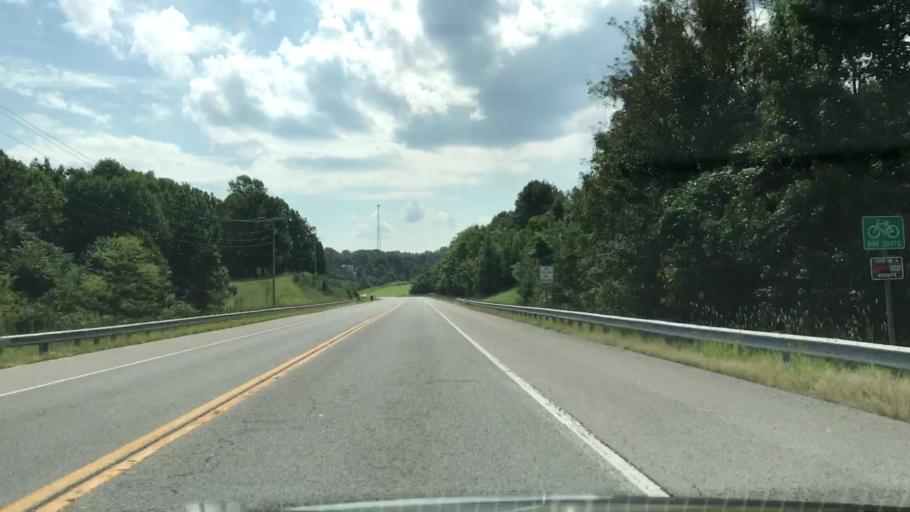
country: US
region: Tennessee
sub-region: Sumner County
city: Westmoreland
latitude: 36.5476
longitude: -86.2219
